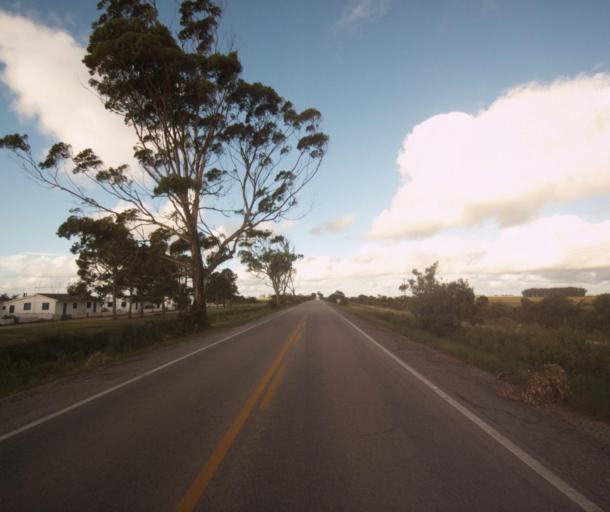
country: BR
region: Rio Grande do Sul
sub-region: Rio Grande
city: Rio Grande
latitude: -32.1946
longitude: -52.4378
